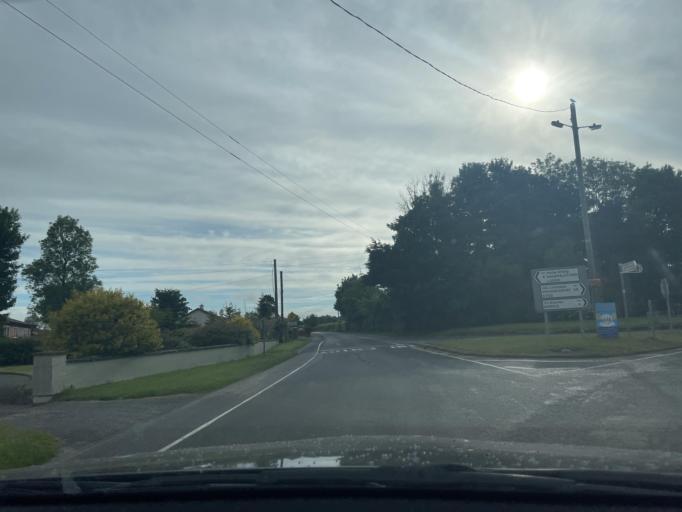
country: IE
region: Leinster
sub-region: County Carlow
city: Bagenalstown
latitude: 52.6329
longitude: -6.9789
